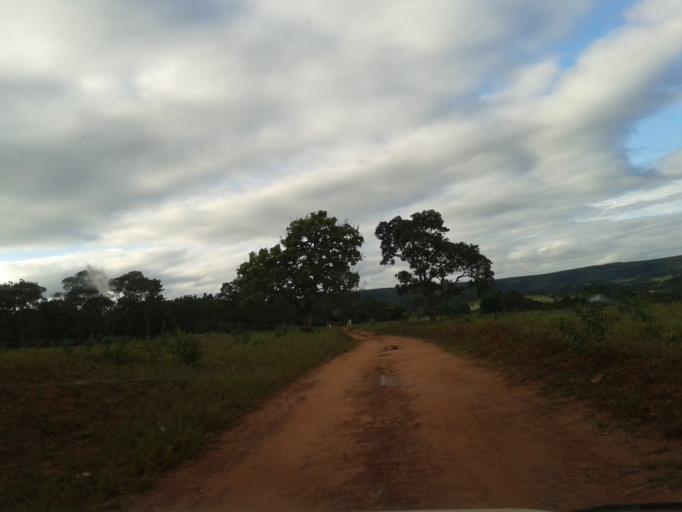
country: BR
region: Minas Gerais
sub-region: Campina Verde
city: Campina Verde
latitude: -19.4842
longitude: -49.6522
